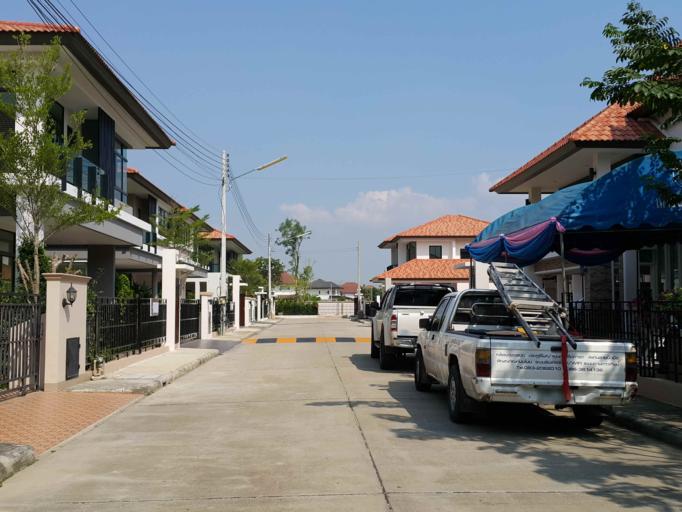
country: TH
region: Chiang Mai
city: Saraphi
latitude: 18.7550
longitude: 99.0412
